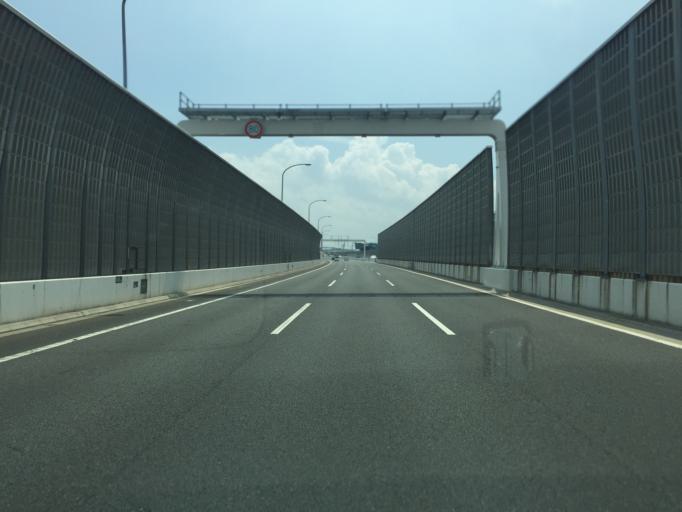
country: JP
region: Kanagawa
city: Yokohama
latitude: 35.4275
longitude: 139.6713
